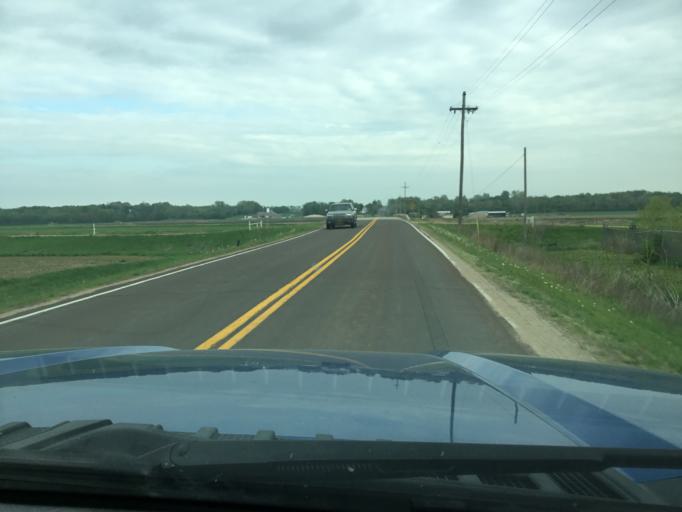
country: US
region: Kansas
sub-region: Shawnee County
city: Topeka
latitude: 39.0965
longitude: -95.7483
